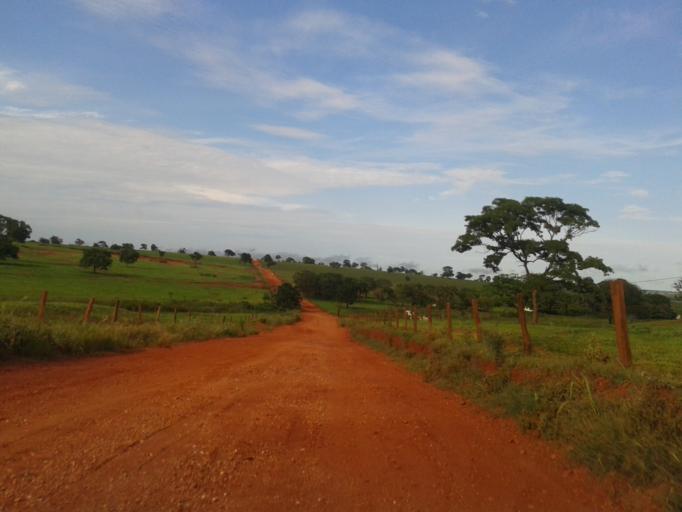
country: BR
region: Minas Gerais
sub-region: Santa Vitoria
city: Santa Vitoria
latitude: -19.1005
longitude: -50.5043
